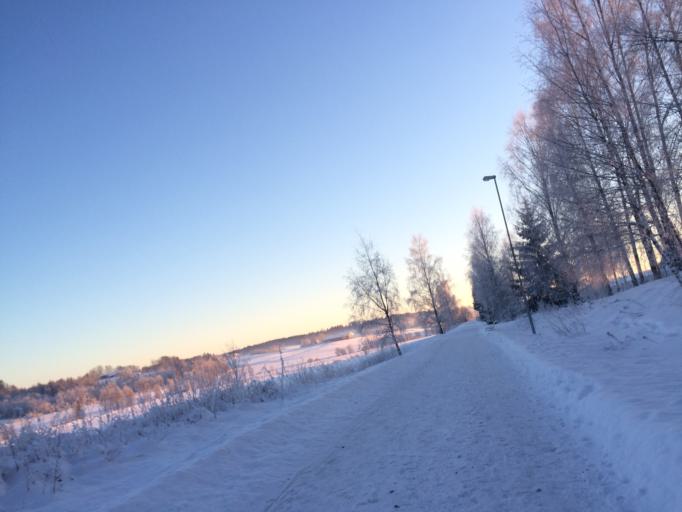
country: NO
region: Akershus
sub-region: Ski
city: Ski
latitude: 59.7001
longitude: 10.8324
